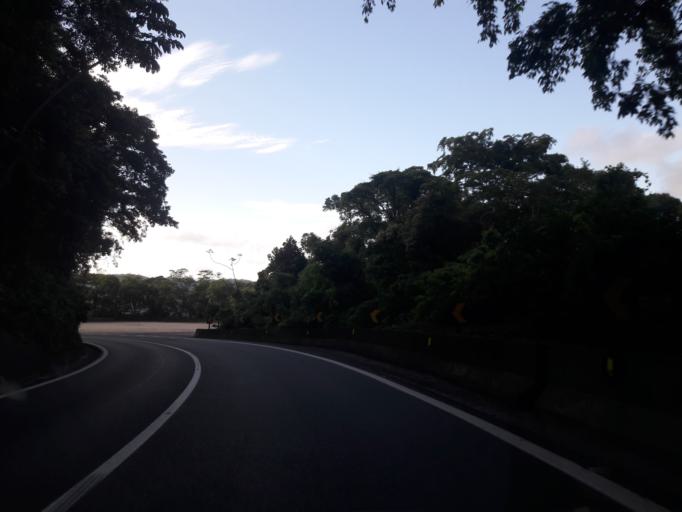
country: BR
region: Sao Paulo
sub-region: Cubatao
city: Cubatao
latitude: -23.8900
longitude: -46.4932
